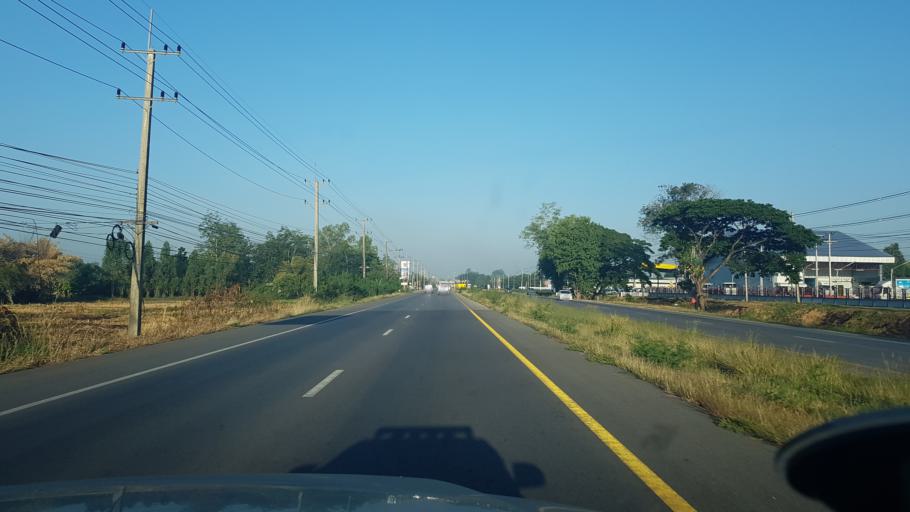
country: TH
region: Khon Kaen
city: Chum Phae
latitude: 16.5822
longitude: 102.0151
